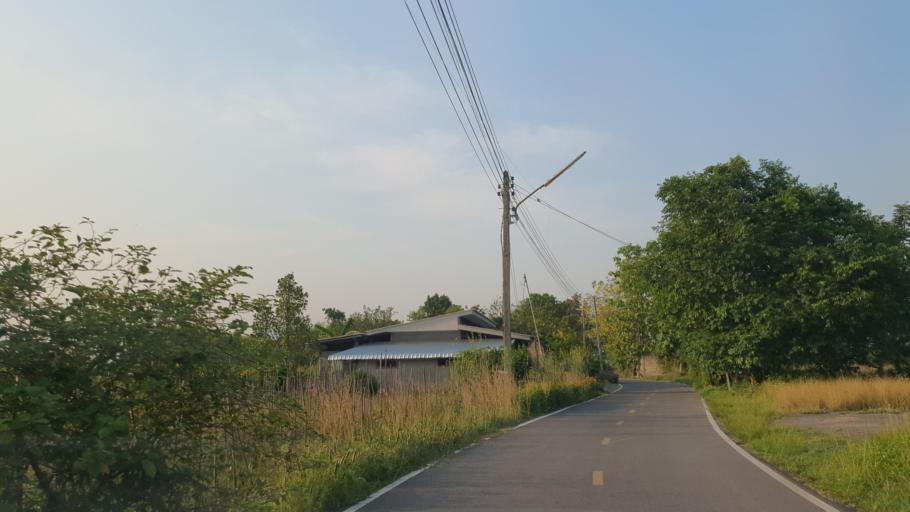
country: TH
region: Chiang Mai
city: San Pa Tong
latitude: 18.6434
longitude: 98.9100
